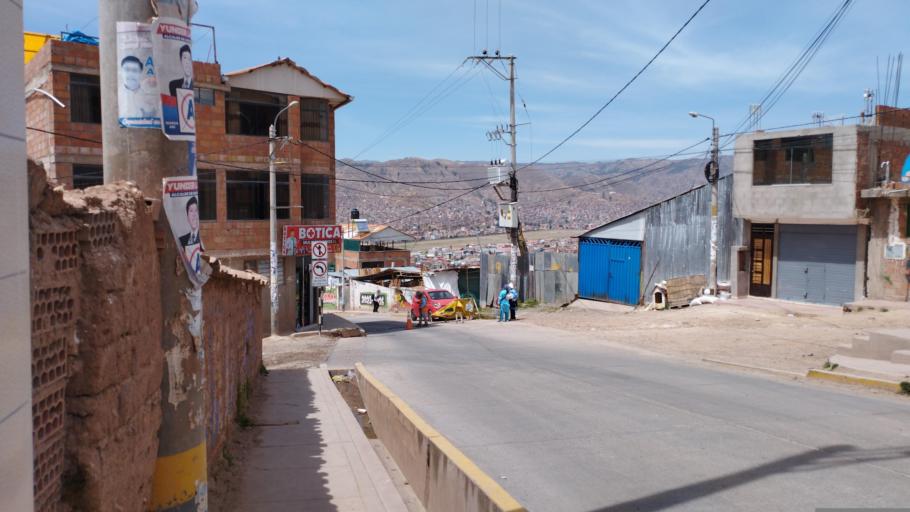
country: PE
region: Cusco
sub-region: Provincia de Cusco
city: Cusco
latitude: -13.5253
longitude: -71.9292
